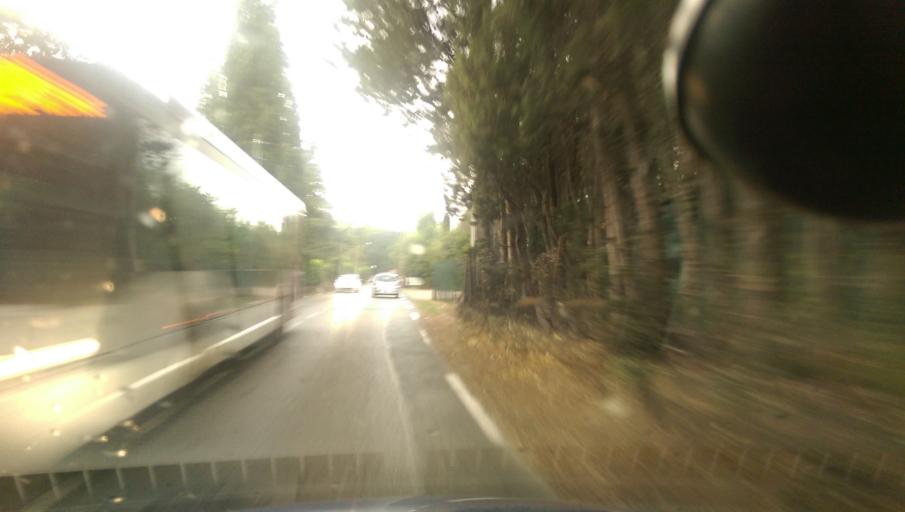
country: FR
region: Provence-Alpes-Cote d'Azur
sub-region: Departement des Alpes-Maritimes
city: Valbonne
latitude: 43.6421
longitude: 7.0289
